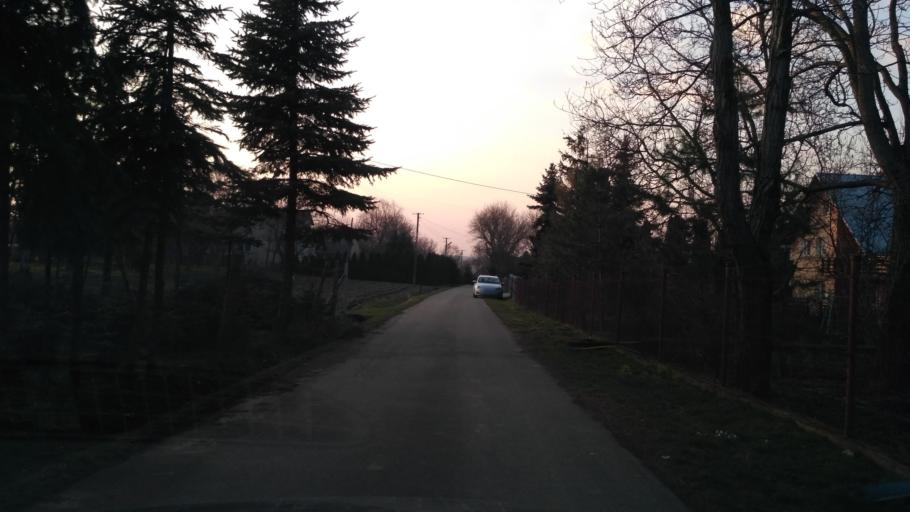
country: PL
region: Subcarpathian Voivodeship
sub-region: Powiat przeworski
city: Zurawiczki
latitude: 50.0067
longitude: 22.4896
